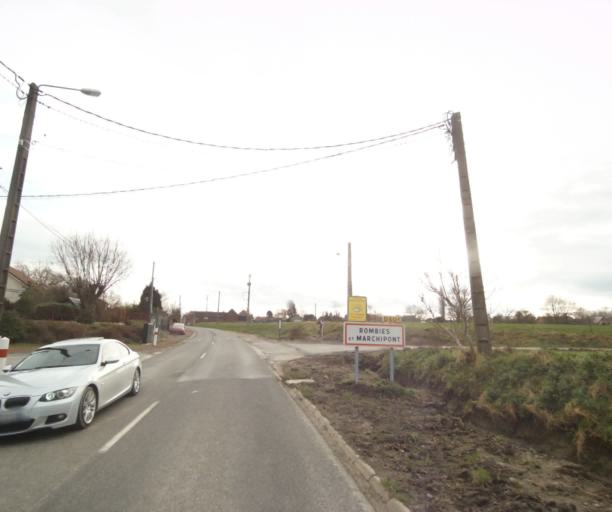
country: FR
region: Nord-Pas-de-Calais
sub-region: Departement du Nord
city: Sebourg
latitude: 50.3677
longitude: 3.6440
